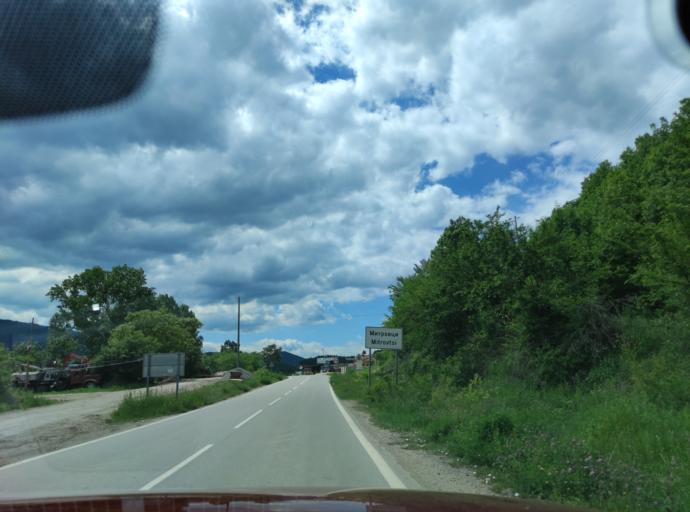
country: BG
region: Montana
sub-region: Obshtina Chiprovtsi
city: Chiprovtsi
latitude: 43.4384
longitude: 22.9420
